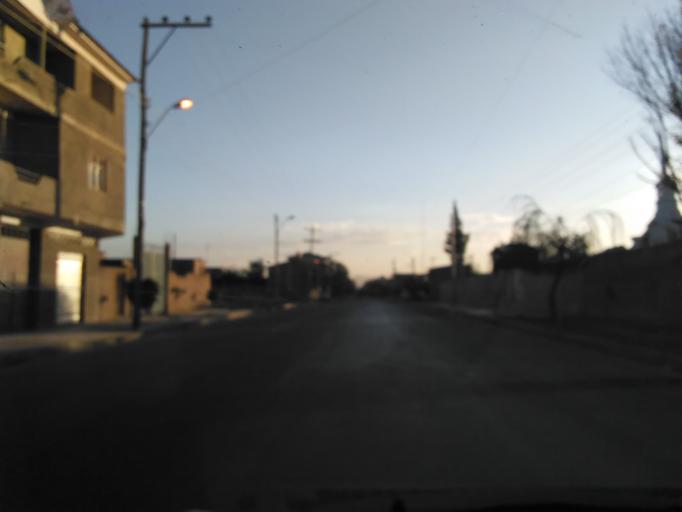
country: BO
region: Cochabamba
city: Punata
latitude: -17.5476
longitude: -65.8311
